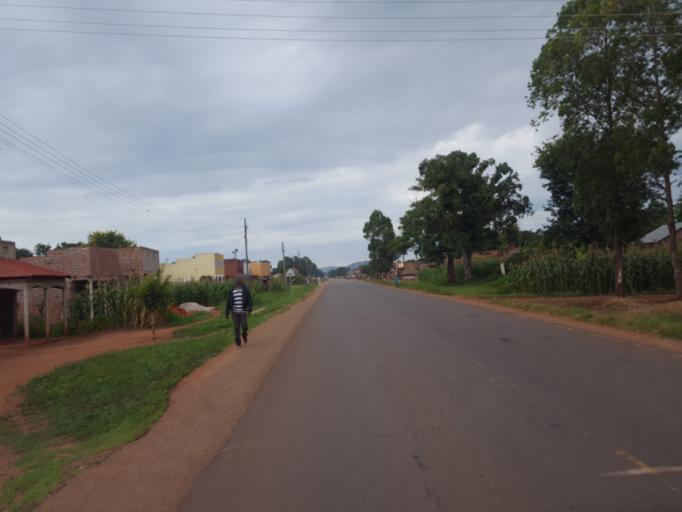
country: UG
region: Central Region
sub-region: Kiboga District
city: Kiboga
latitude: 1.0317
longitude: 31.6778
